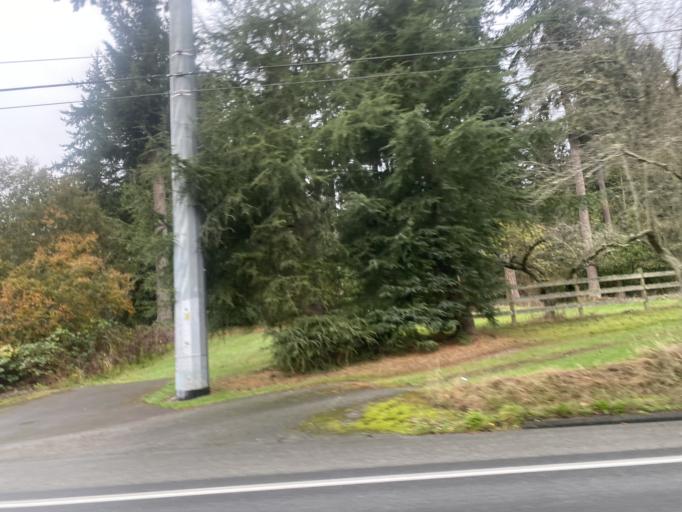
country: US
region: Washington
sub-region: Island County
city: Camano
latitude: 48.0952
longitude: -122.5715
